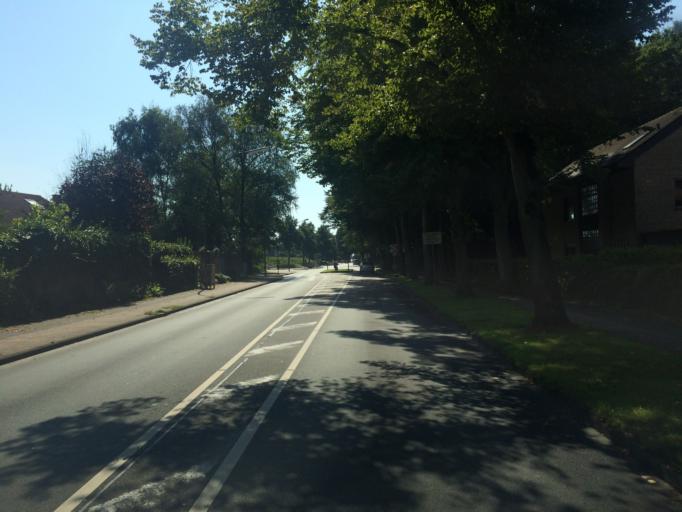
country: DE
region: North Rhine-Westphalia
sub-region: Regierungsbezirk Munster
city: Muenster
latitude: 51.9825
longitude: 7.7025
